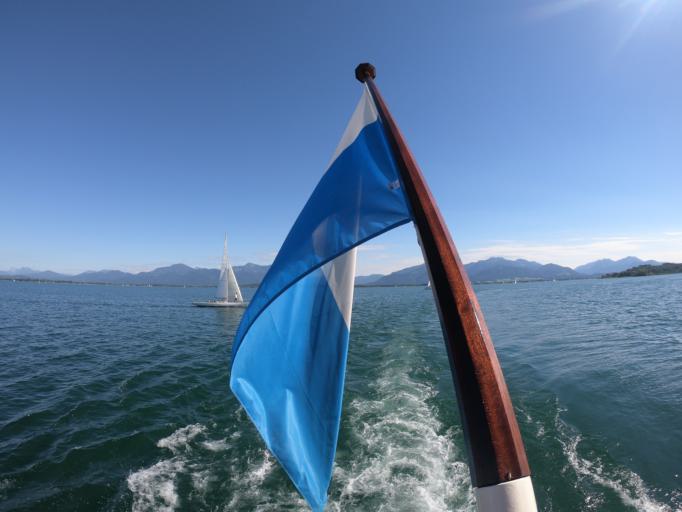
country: DE
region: Bavaria
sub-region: Upper Bavaria
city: Chiemsee
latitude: 47.8696
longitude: 12.4290
